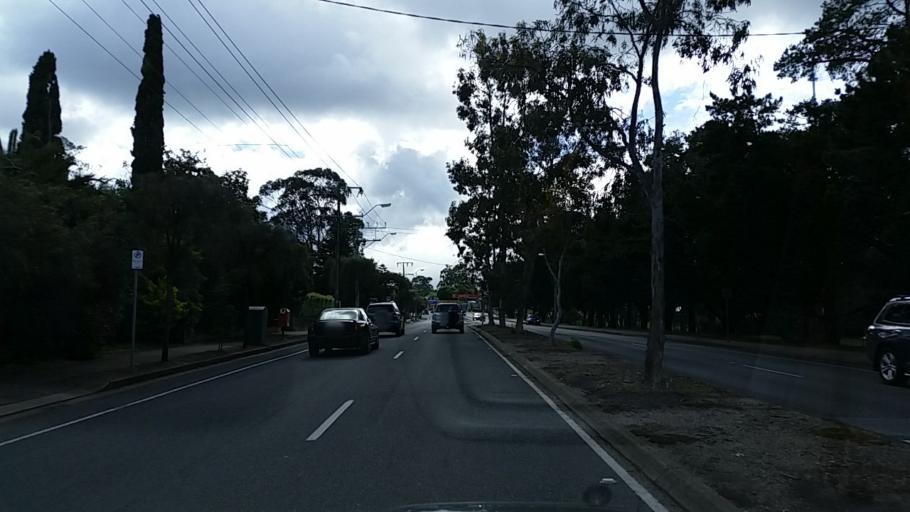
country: AU
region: South Australia
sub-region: Mitcham
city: Blackwood
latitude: -35.0271
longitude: 138.6007
